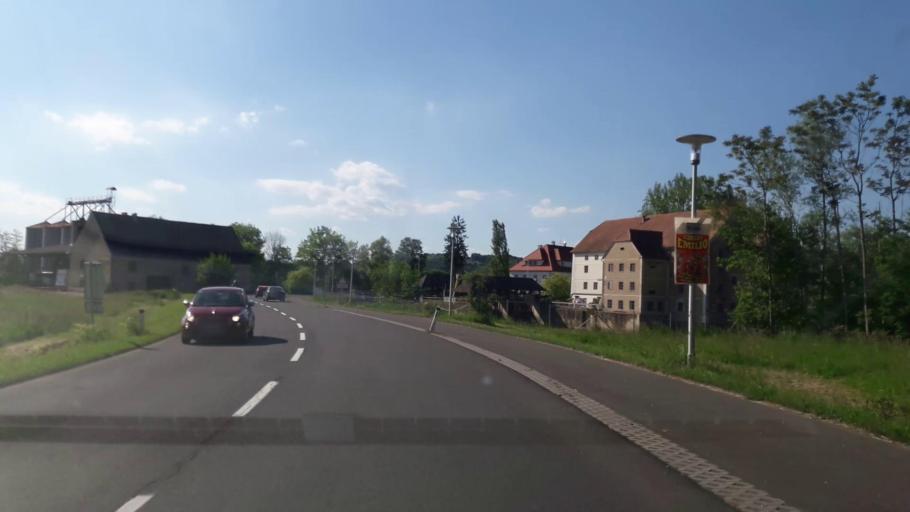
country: AT
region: Styria
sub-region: Politischer Bezirk Suedoststeiermark
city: Fehring
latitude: 46.9441
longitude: 16.0104
